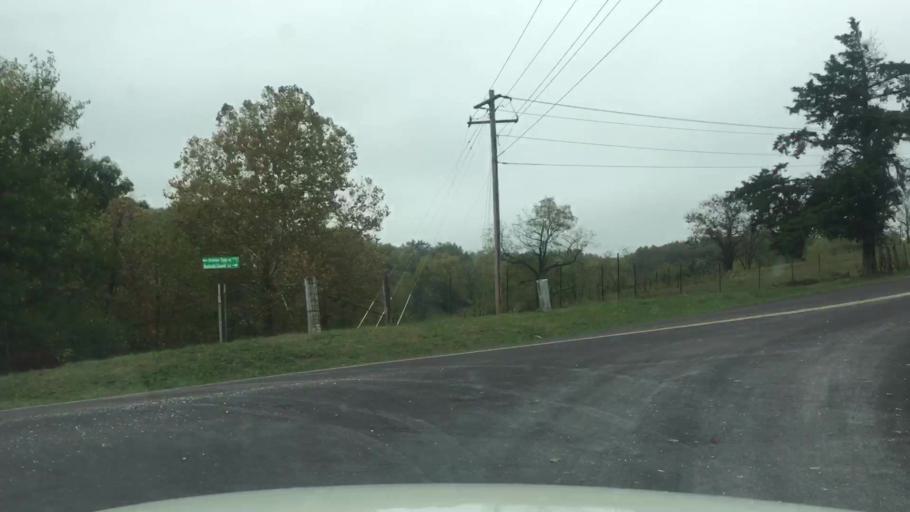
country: US
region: Missouri
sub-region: Boone County
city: Ashland
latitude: 38.8205
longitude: -92.3470
